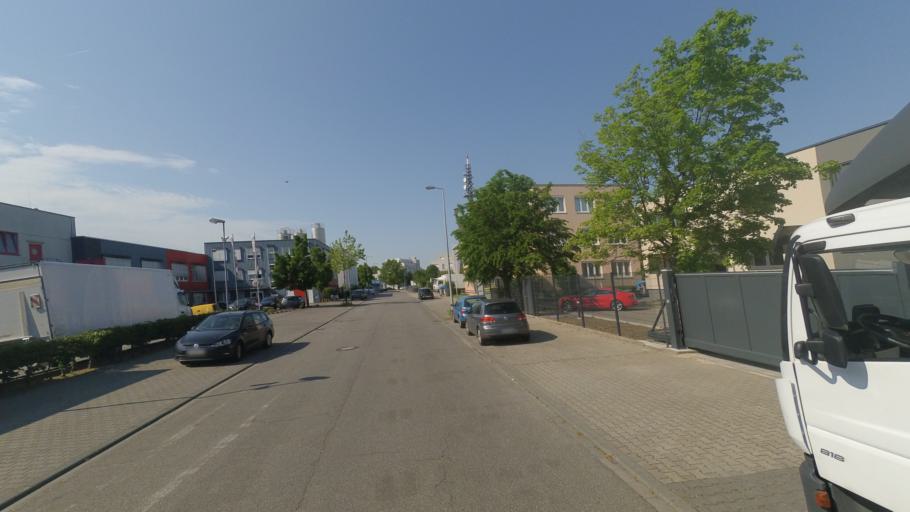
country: DE
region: Rheinland-Pfalz
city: Altrip
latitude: 49.4508
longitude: 8.5179
